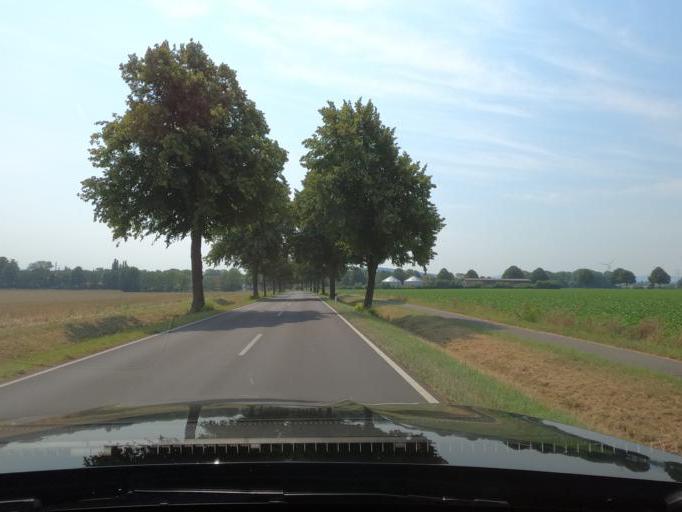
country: DE
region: Lower Saxony
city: Nordstemmen
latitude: 52.2037
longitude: 9.7867
